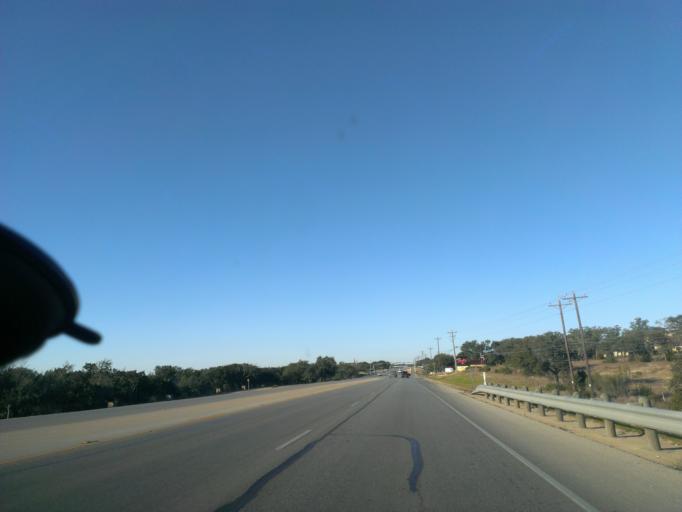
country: US
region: Texas
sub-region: Hays County
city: Dripping Springs
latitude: 30.2047
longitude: -97.9816
